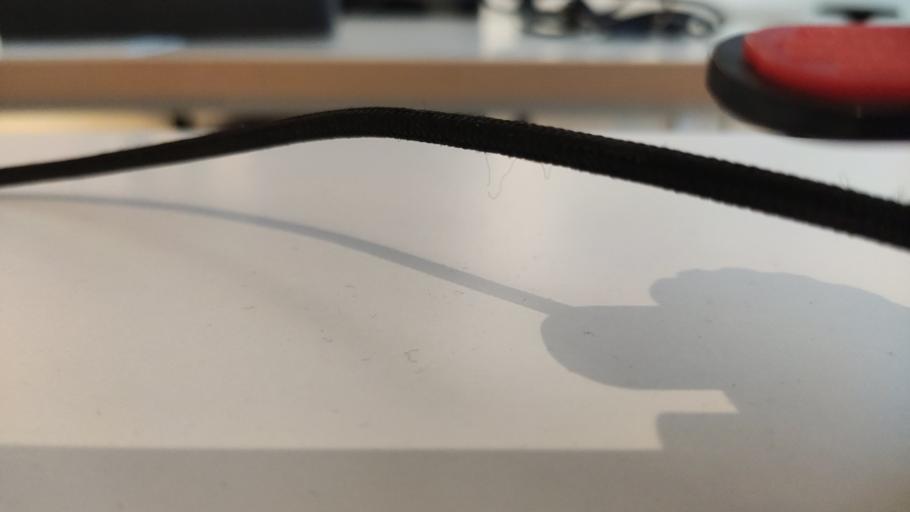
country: RU
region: Moskovskaya
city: Novopetrovskoye
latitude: 55.8988
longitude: 36.4336
